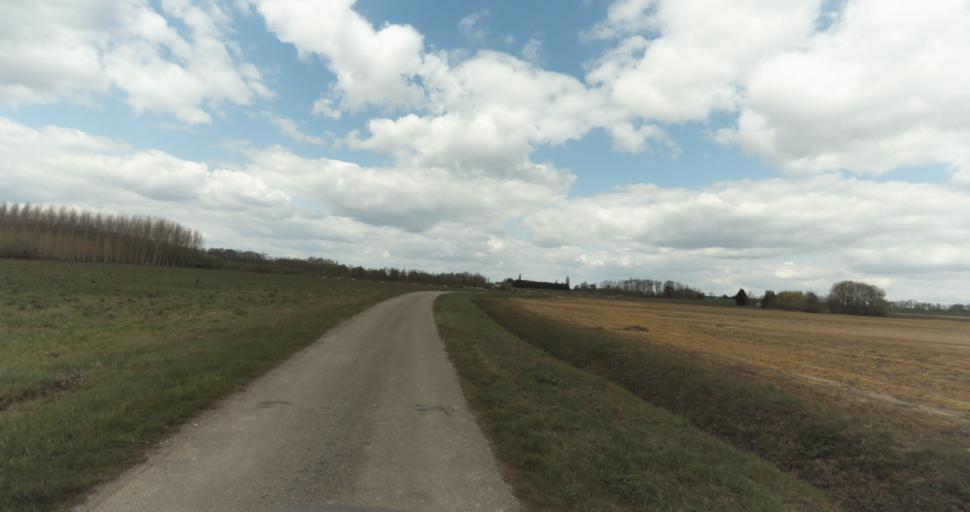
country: FR
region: Bourgogne
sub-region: Departement de la Cote-d'Or
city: Auxonne
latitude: 47.1683
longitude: 5.3941
